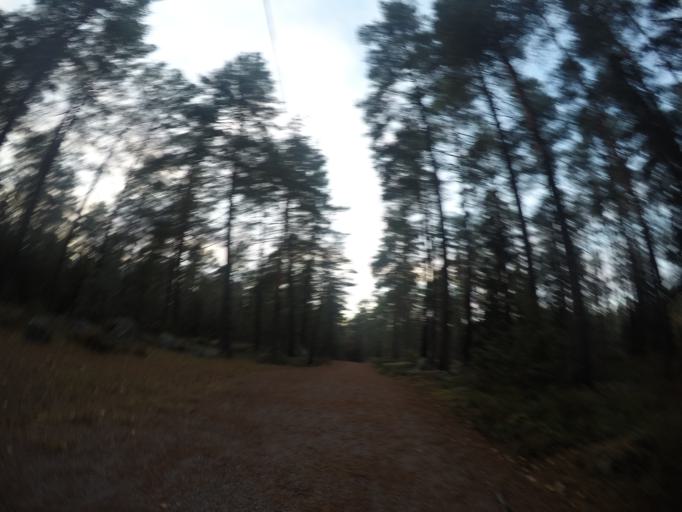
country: SE
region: Soedermanland
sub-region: Eskilstuna Kommun
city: Eskilstuna
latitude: 59.3450
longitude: 16.5193
